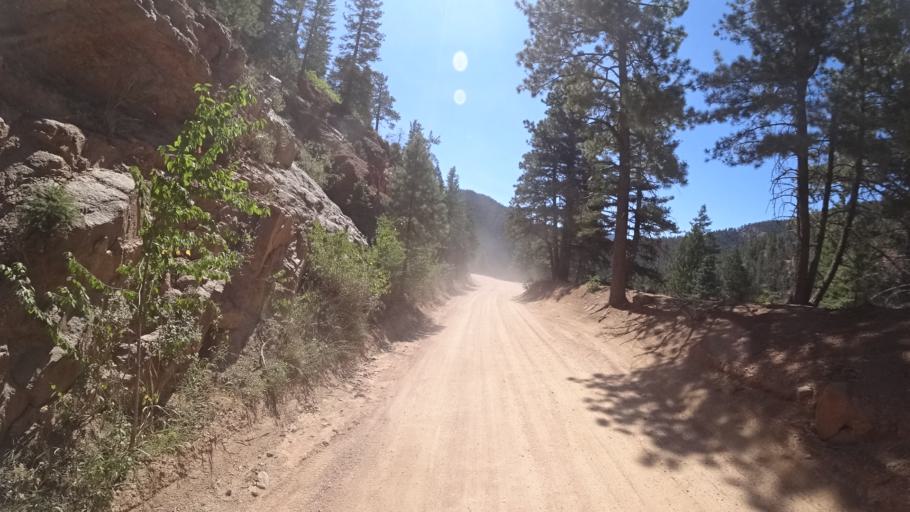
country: US
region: Colorado
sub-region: El Paso County
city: Manitou Springs
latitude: 38.7944
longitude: -104.8962
